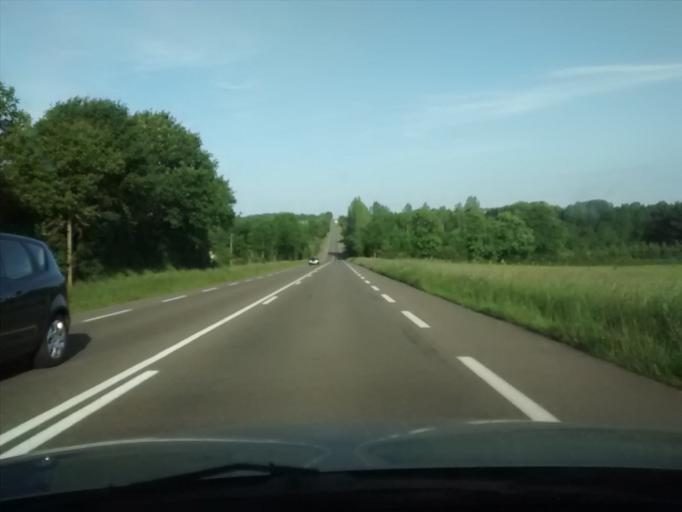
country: FR
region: Pays de la Loire
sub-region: Departement de la Mayenne
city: Soulge-sur-Ouette
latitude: 48.0533
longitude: -0.5422
